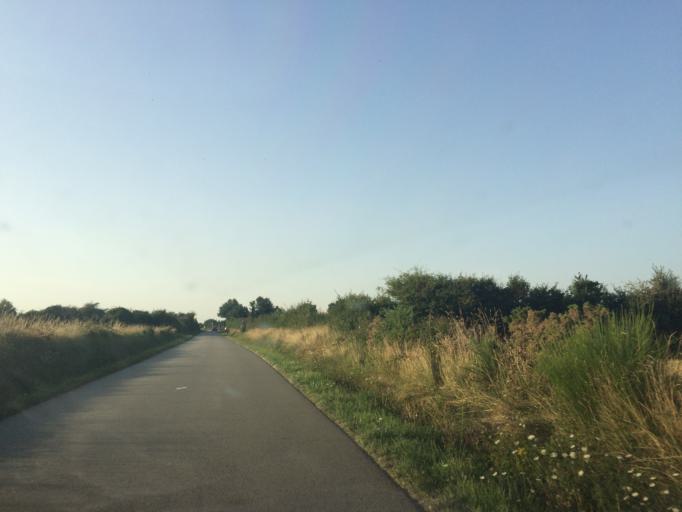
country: FR
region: Brittany
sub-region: Departement du Morbihan
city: Ambon
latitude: 47.5290
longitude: -2.5543
